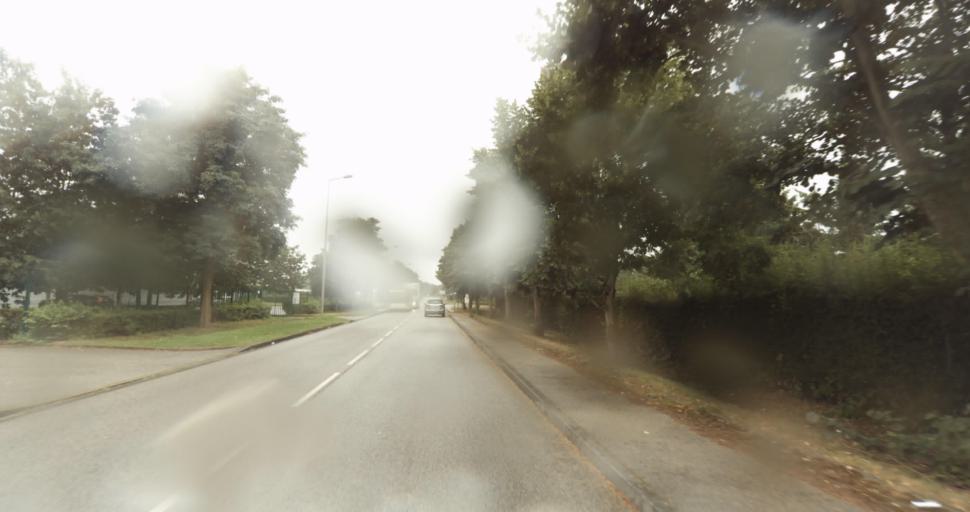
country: FR
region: Haute-Normandie
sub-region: Departement de l'Eure
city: Evreux
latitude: 49.0084
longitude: 1.1746
